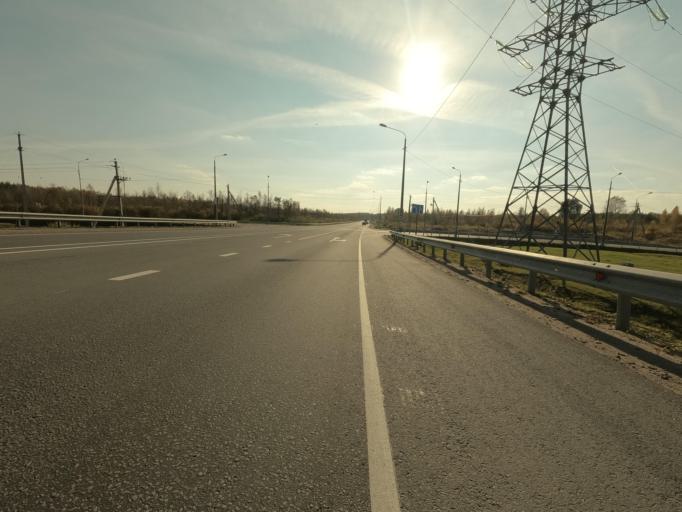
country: RU
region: Leningrad
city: Mga
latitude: 59.7502
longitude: 31.0892
